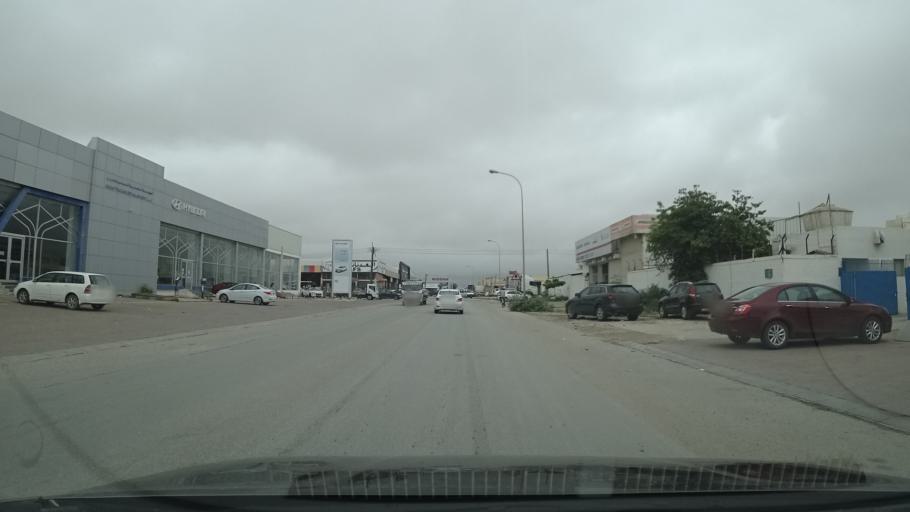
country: OM
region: Zufar
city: Salalah
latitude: 17.0162
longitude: 54.0452
